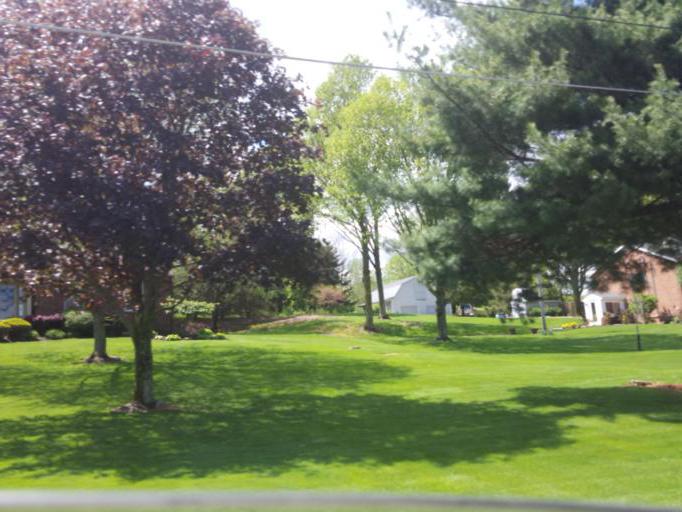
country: US
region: Ohio
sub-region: Richland County
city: Ontario
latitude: 40.7443
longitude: -82.5710
